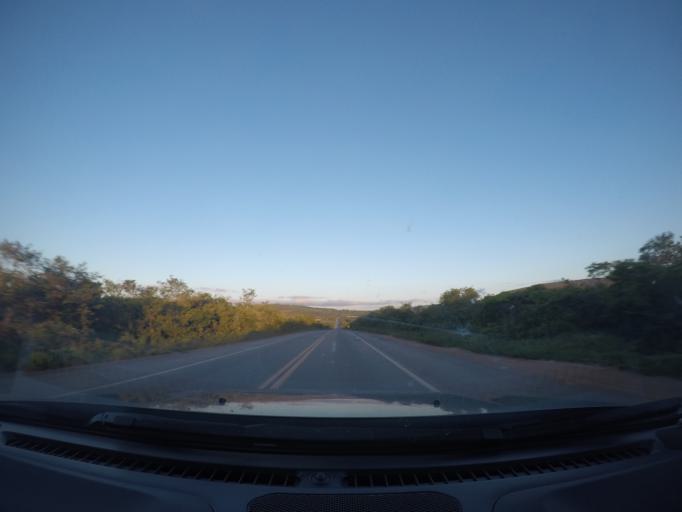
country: BR
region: Bahia
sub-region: Seabra
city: Seabra
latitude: -12.3906
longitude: -41.9034
